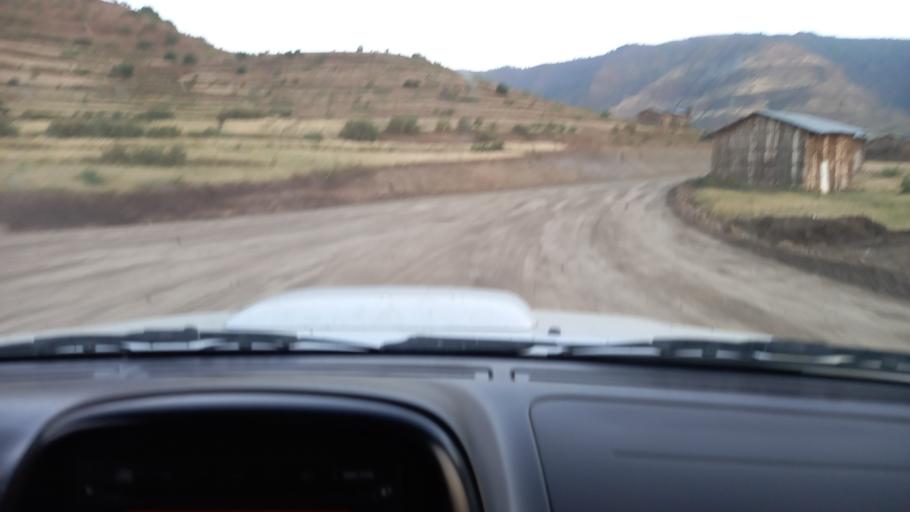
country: ET
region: Amhara
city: Debark'
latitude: 13.0377
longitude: 38.0401
